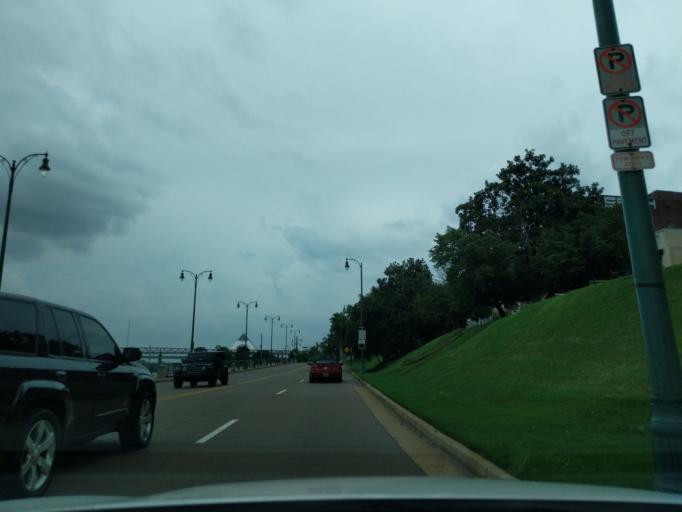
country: US
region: Tennessee
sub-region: Shelby County
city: Memphis
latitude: 35.1422
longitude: -90.0572
